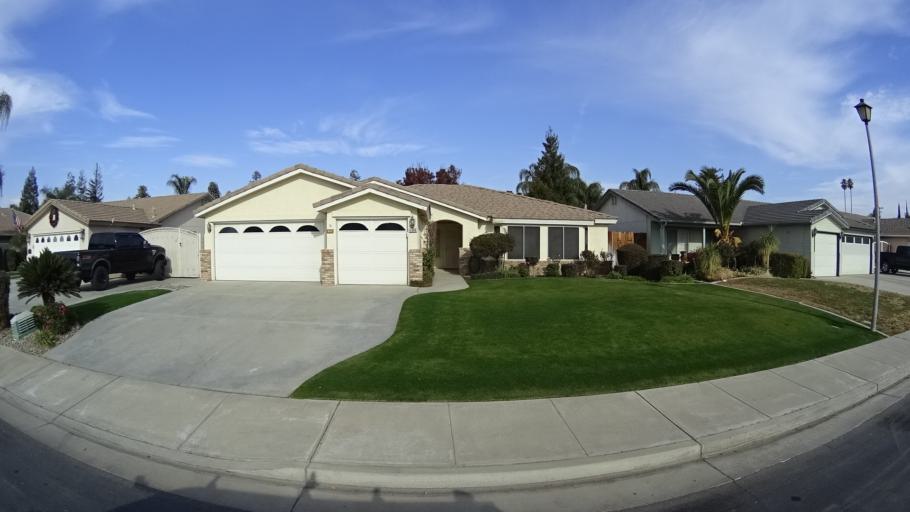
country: US
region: California
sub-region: Kern County
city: Greenacres
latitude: 35.4082
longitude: -119.0681
